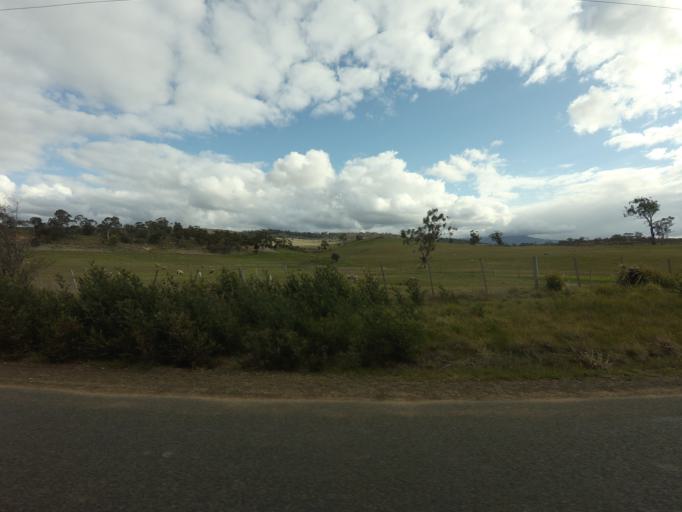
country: AU
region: Tasmania
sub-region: Northern Midlands
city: Evandale
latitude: -41.8844
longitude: 147.3118
